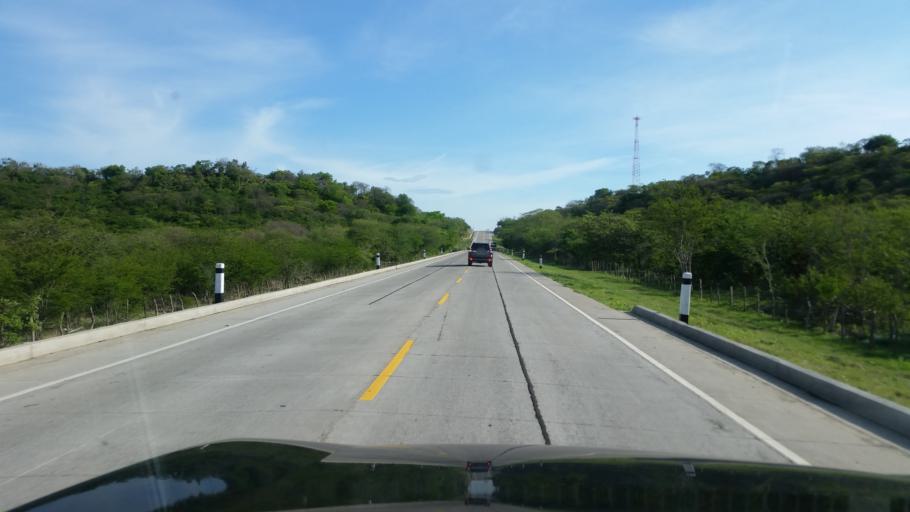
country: NI
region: Leon
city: Nagarote
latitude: 12.2008
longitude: -86.6793
